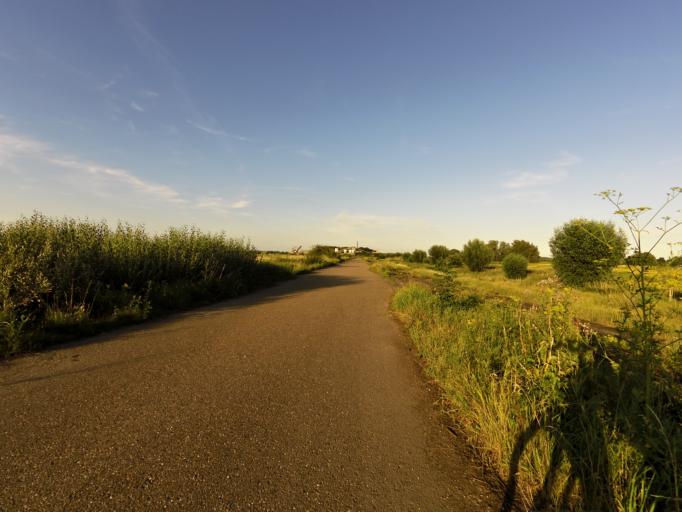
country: NL
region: Gelderland
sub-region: Gemeente Nijmegen
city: Nijmegen
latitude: 51.8743
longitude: 5.8965
